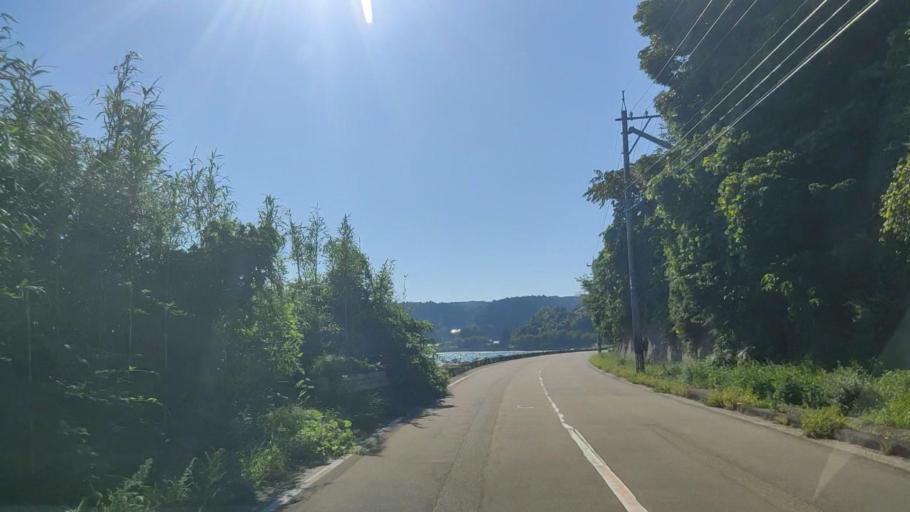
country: JP
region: Ishikawa
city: Nanao
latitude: 37.2798
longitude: 137.1043
